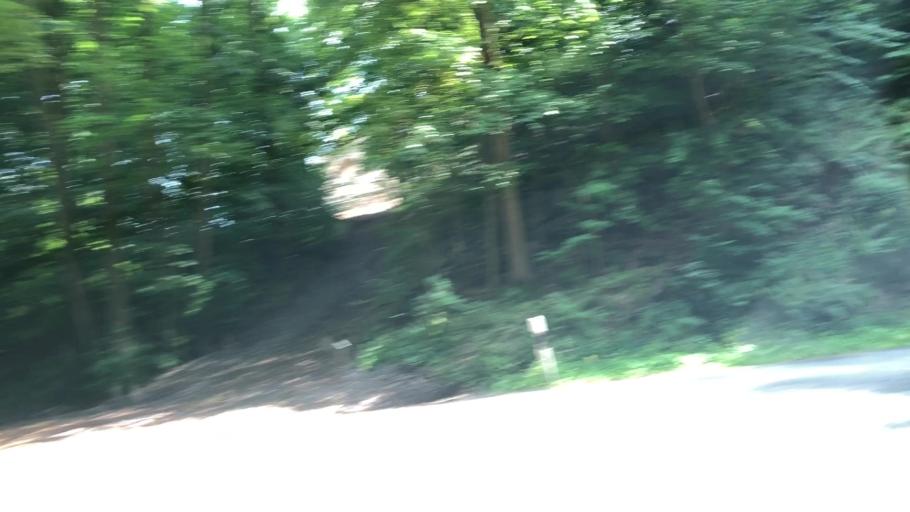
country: DE
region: North Rhine-Westphalia
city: Porta Westfalica
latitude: 52.2463
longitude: 8.9050
